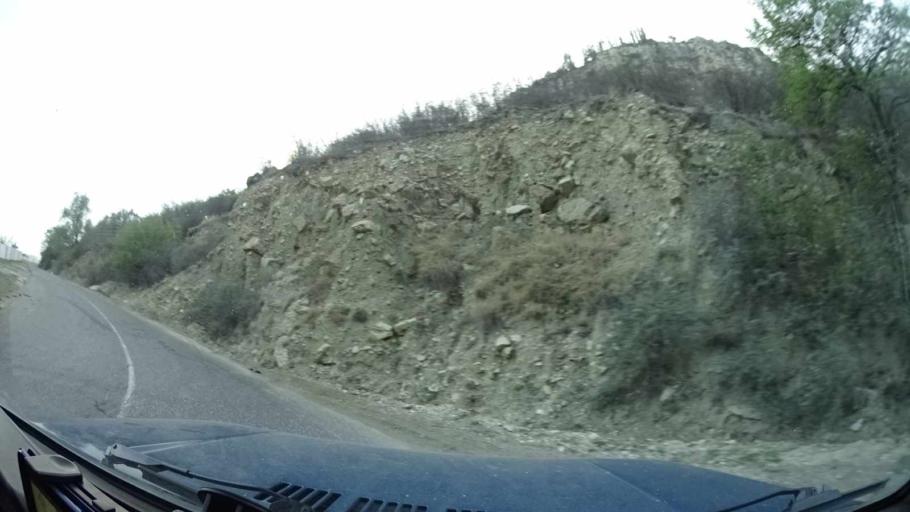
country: RU
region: Dagestan
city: Gunib
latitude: 42.3854
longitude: 46.9688
